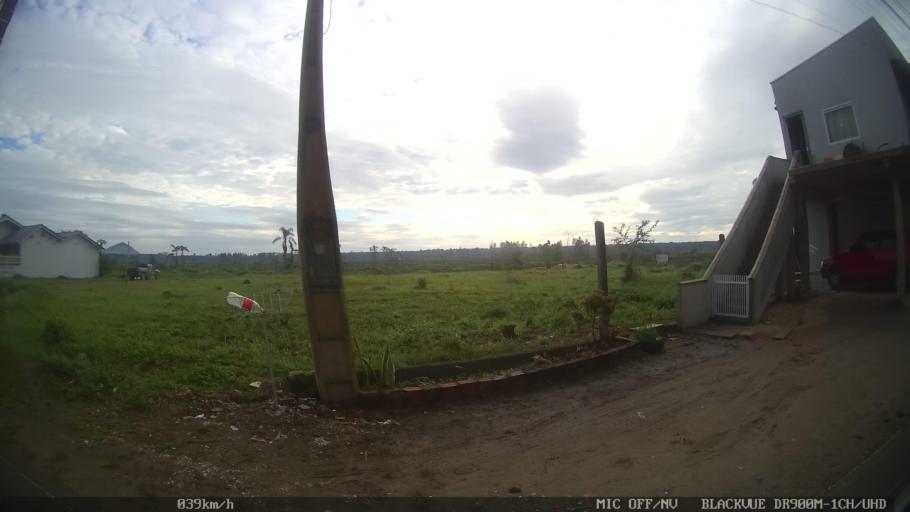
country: BR
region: Santa Catarina
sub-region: Barra Velha
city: Barra Velha
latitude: -26.6239
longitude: -48.7039
